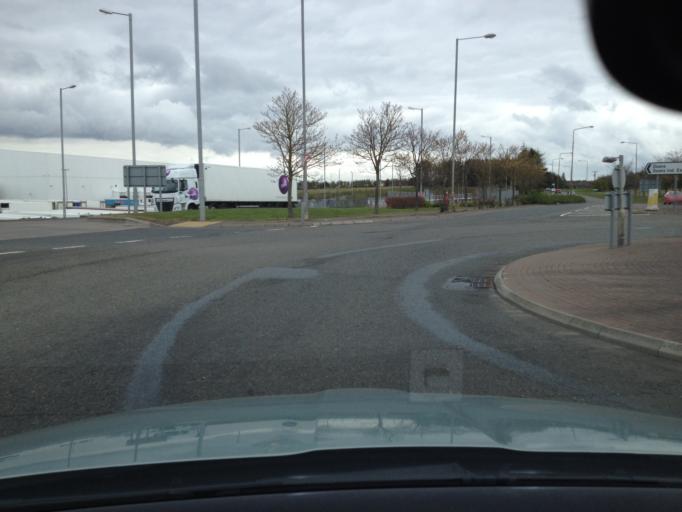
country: GB
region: Scotland
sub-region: West Lothian
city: West Calder
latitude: 55.9026
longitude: -3.5822
